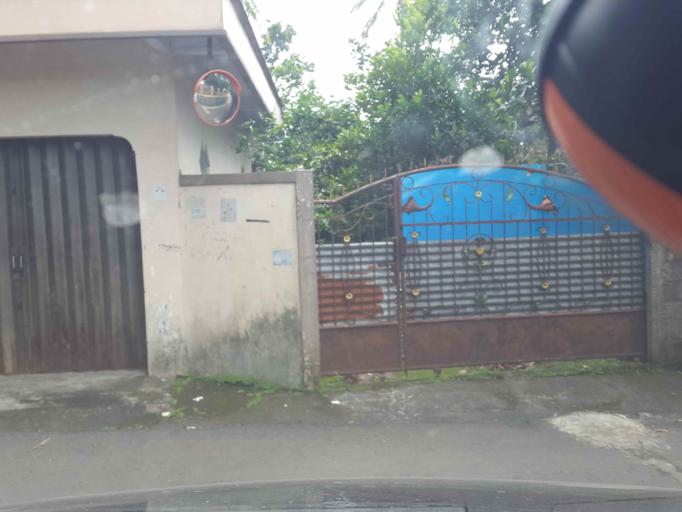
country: ID
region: Central Java
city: Salatiga
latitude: -7.3134
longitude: 110.4912
